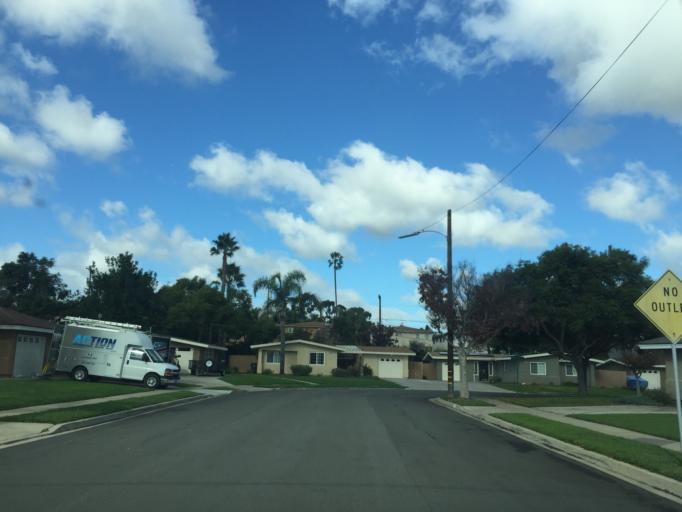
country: US
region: California
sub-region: San Diego County
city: La Jolla
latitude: 32.7991
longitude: -117.2279
